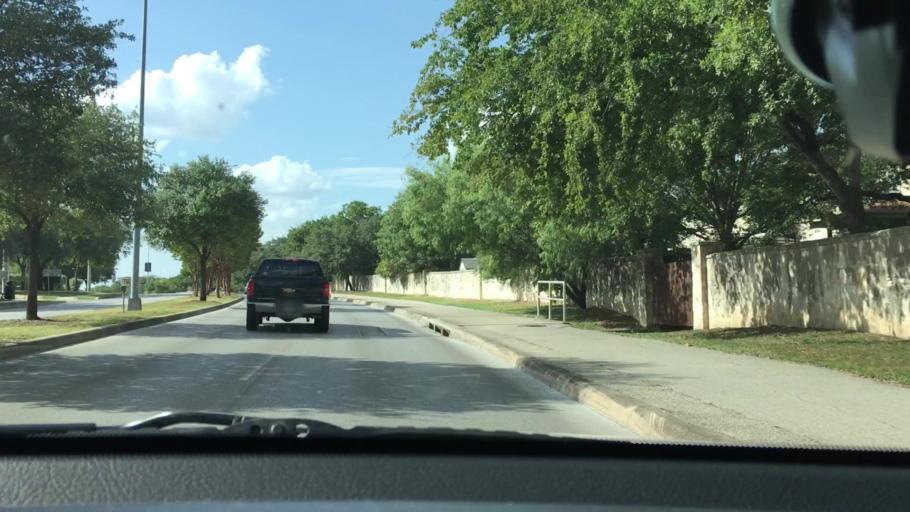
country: US
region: Texas
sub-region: Bexar County
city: Selma
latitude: 29.5801
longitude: -98.2812
